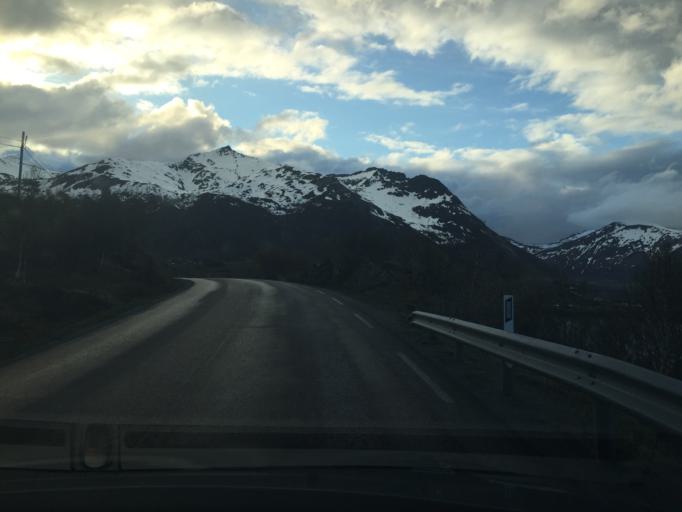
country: NO
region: Nordland
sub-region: Vagan
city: Svolvaer
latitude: 68.3162
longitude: 14.7143
